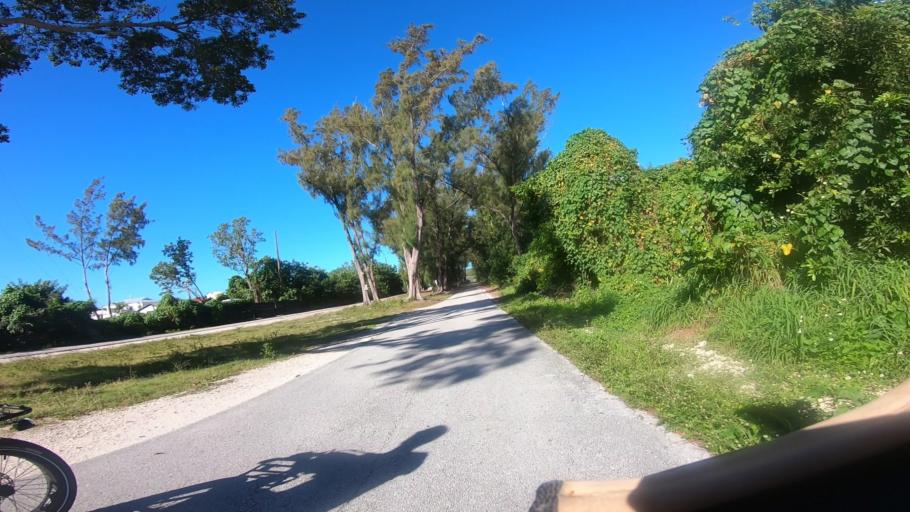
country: US
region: Florida
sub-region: Monroe County
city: Key Largo
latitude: 25.1118
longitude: -80.4275
